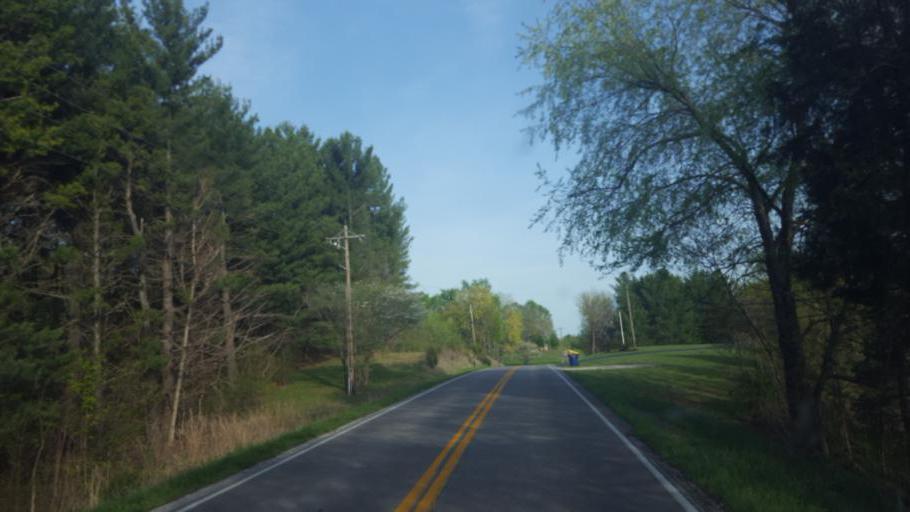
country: US
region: Kentucky
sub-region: Warren County
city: Plano
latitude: 36.9331
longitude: -86.2994
